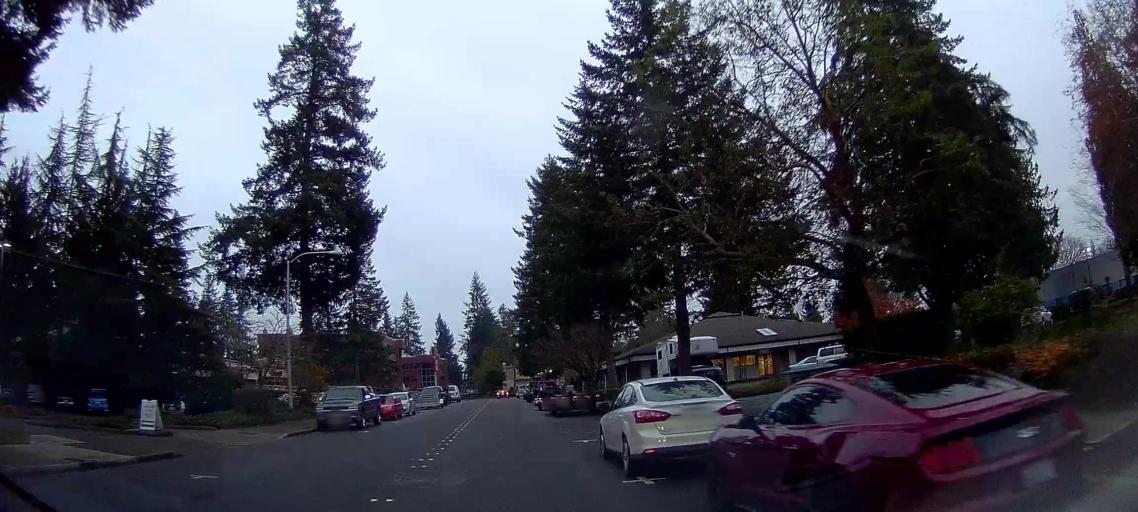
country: US
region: Washington
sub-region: Thurston County
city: Lacey
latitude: 47.0443
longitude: -122.8284
